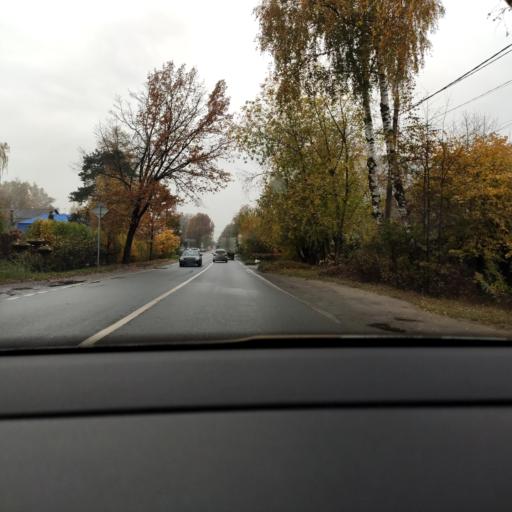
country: RU
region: Moskovskaya
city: Druzhba
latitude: 55.8857
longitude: 37.7510
